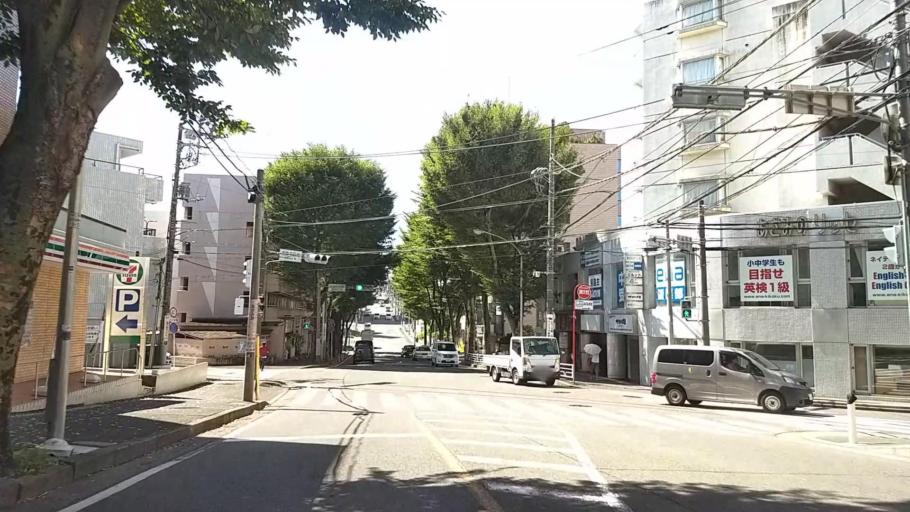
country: JP
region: Tokyo
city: Chofugaoka
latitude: 35.5707
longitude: 139.5547
